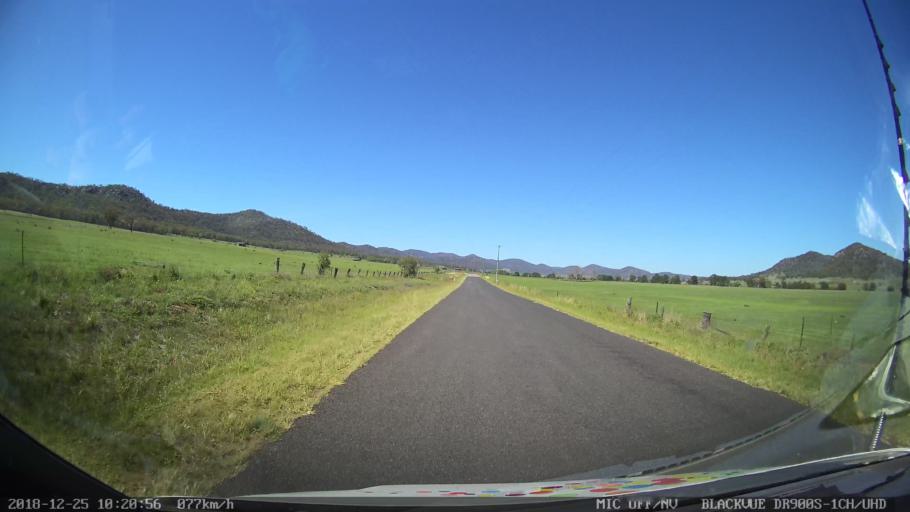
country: AU
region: New South Wales
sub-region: Muswellbrook
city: Denman
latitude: -32.3623
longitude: 150.5446
